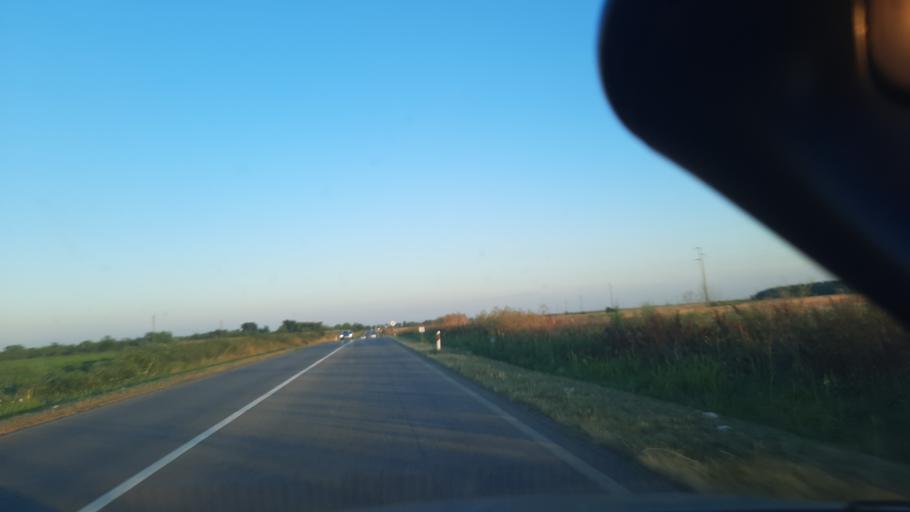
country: RS
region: Autonomna Pokrajina Vojvodina
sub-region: Sremski Okrug
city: Ingija
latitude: 45.0765
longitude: 20.0510
